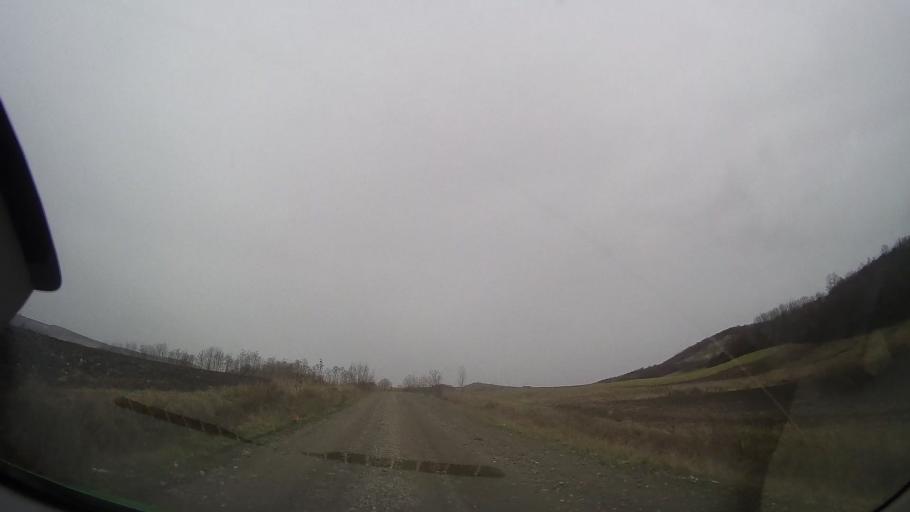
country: RO
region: Mures
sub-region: Comuna Ceausu de Campie
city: Ceausu de Campie
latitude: 46.6541
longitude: 24.4931
